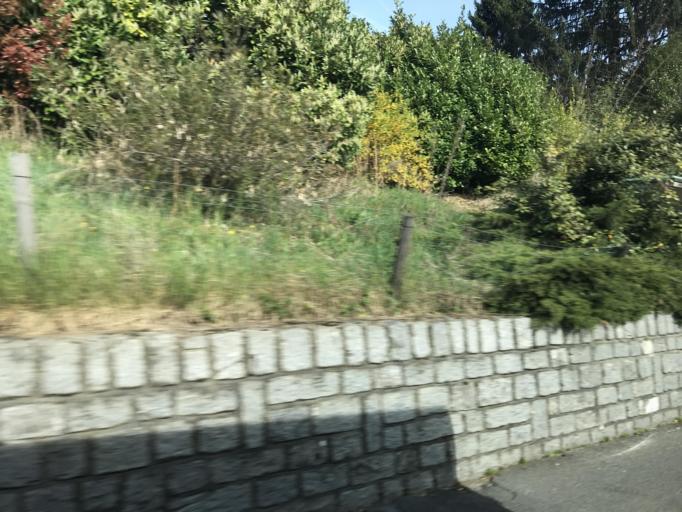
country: CH
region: Ticino
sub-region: Lugano District
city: Sorengo
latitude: 45.9977
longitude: 8.9384
